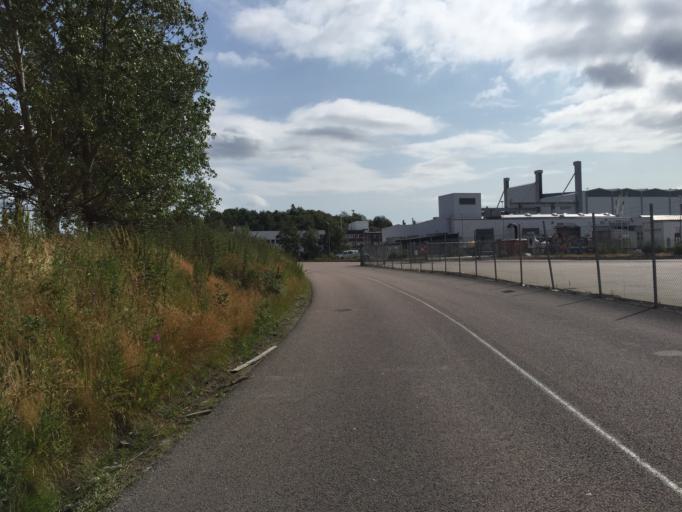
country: SE
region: Vaestra Goetaland
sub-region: Goteborg
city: Torslanda
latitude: 57.6999
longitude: 11.8274
